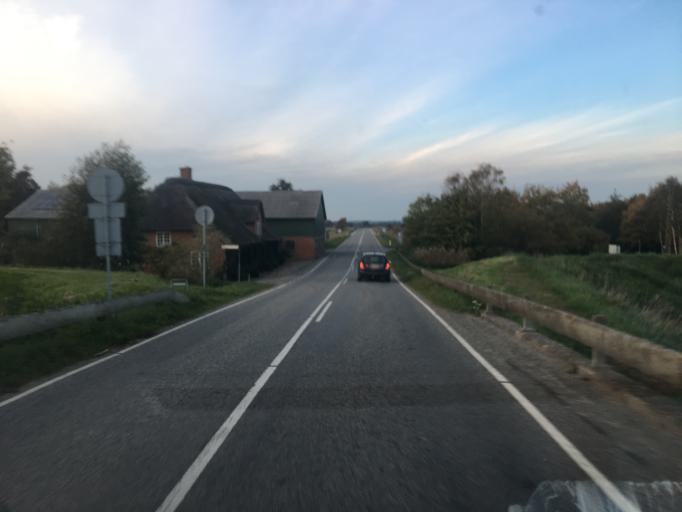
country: DE
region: Schleswig-Holstein
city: Aventoft
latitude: 54.9123
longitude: 8.8330
